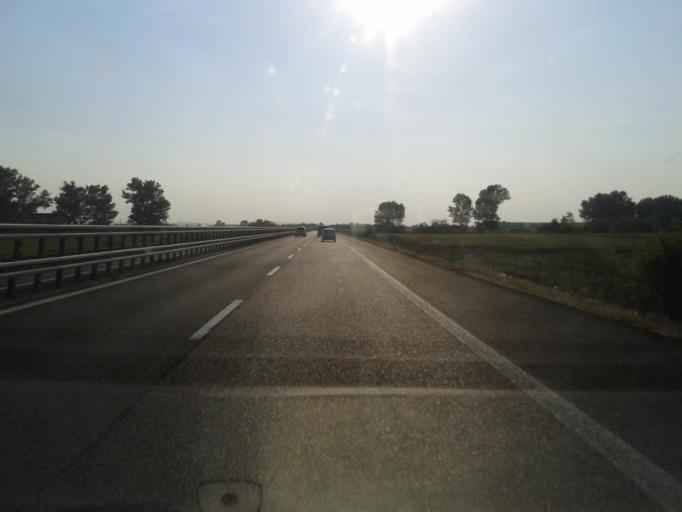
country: IT
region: Emilia-Romagna
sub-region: Provincia di Piacenza
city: Rottofreno
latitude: 45.0654
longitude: 9.5502
